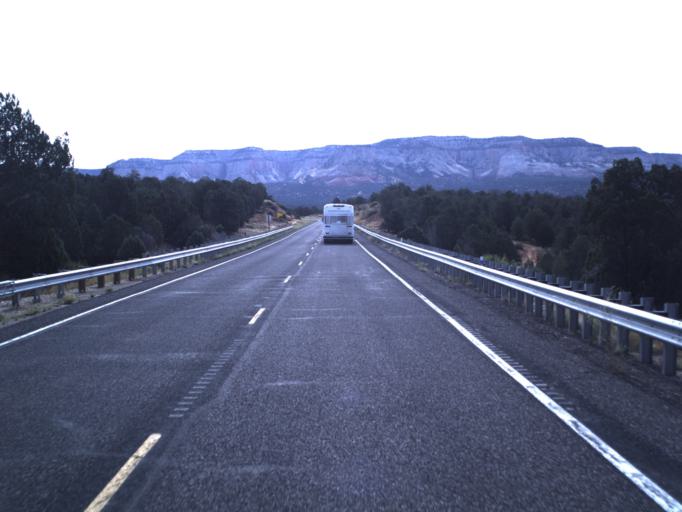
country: US
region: Utah
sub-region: Kane County
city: Kanab
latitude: 37.2199
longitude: -112.7019
